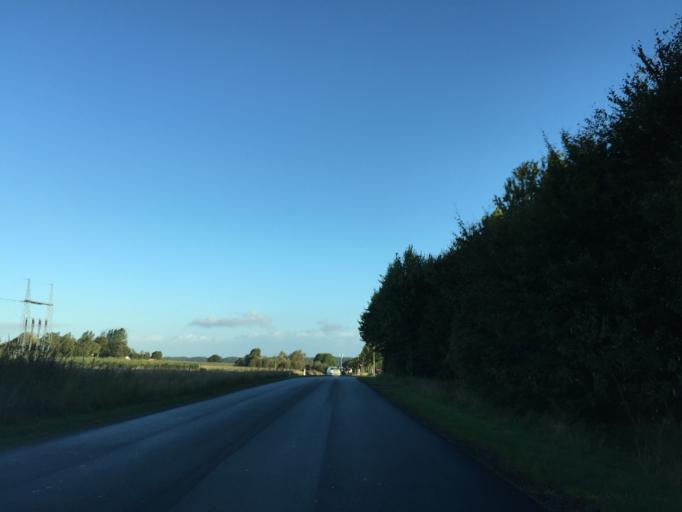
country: DK
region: Central Jutland
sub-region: Viborg Kommune
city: Bjerringbro
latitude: 56.3568
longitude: 9.6683
